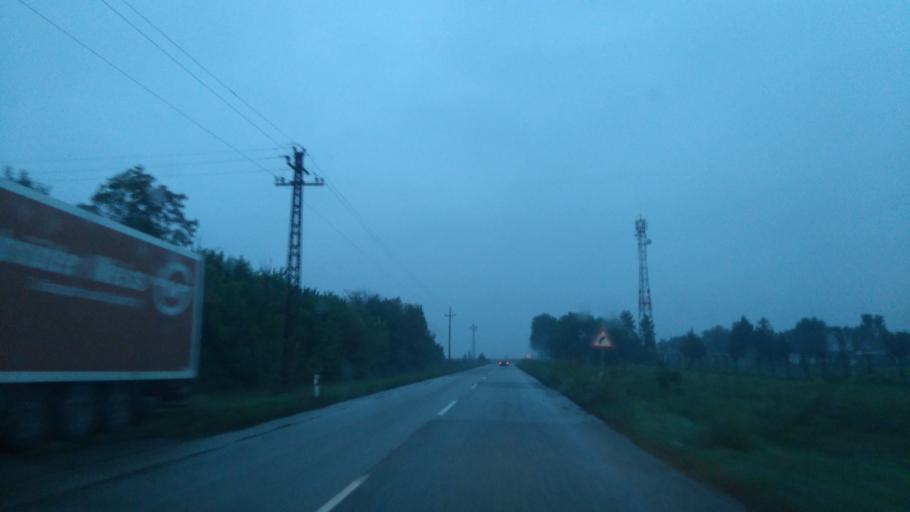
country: RS
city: Backo Petrovo Selo
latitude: 45.7226
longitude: 20.0952
